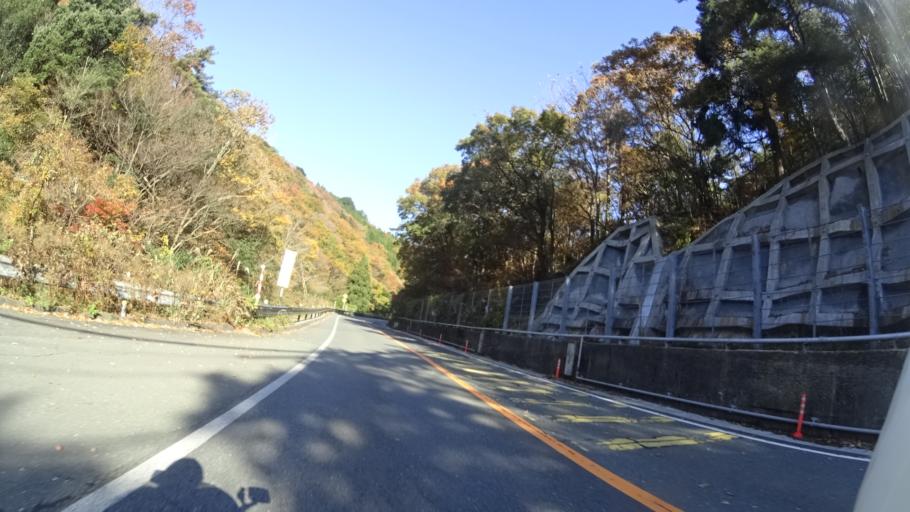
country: JP
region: Fukui
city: Tsuruga
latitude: 35.5254
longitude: 136.0955
